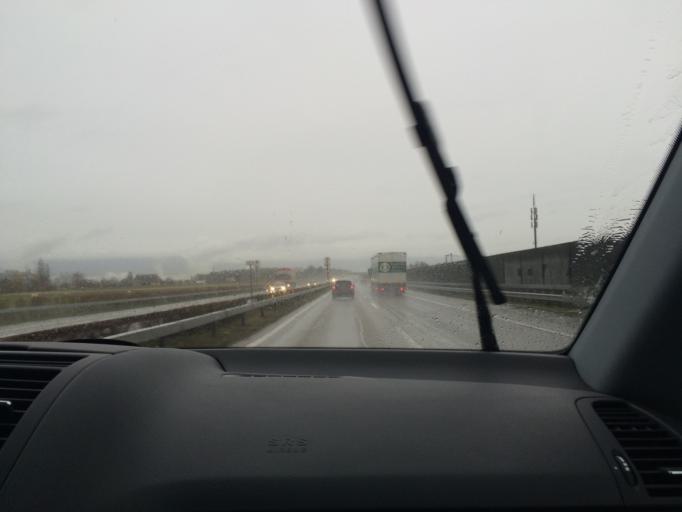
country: CH
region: Bern
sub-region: Emmental District
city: Kirchberg
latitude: 47.0951
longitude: 7.5737
